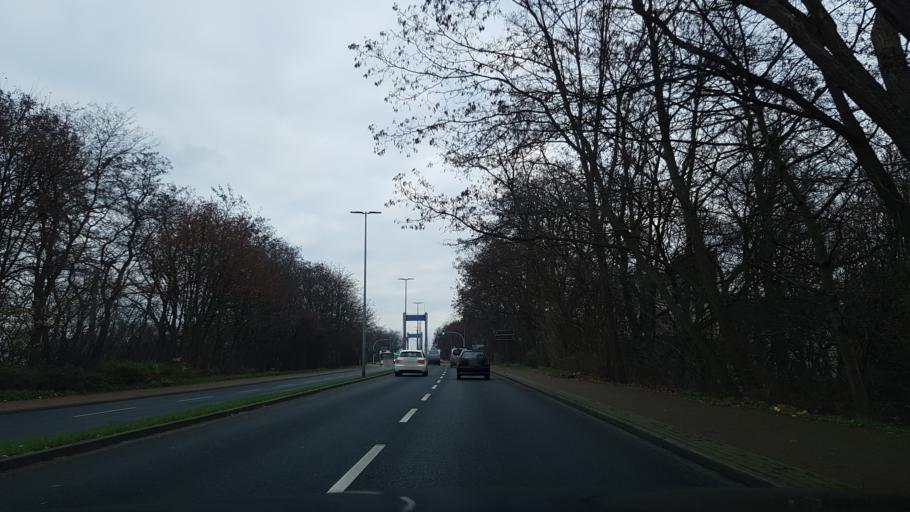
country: DE
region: North Rhine-Westphalia
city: Meiderich
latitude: 51.4570
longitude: 6.7139
